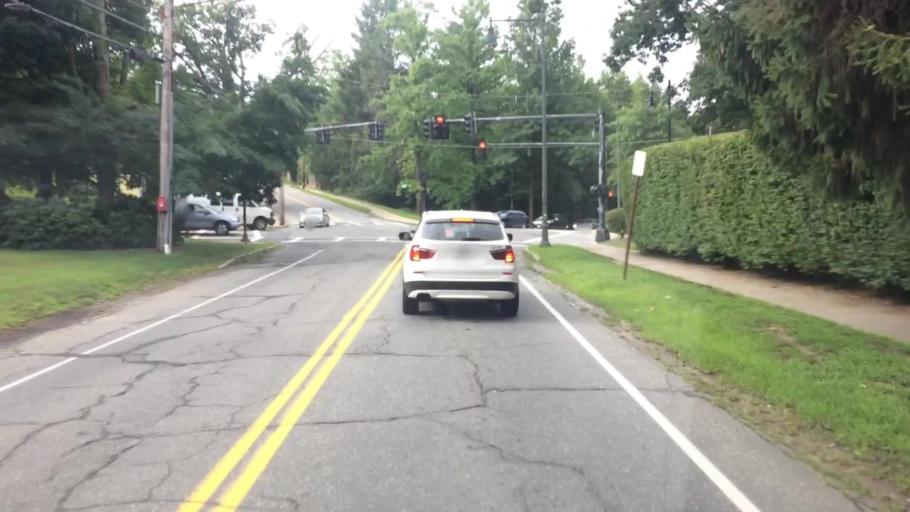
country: US
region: Massachusetts
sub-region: Middlesex County
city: Winchester
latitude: 42.4531
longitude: -71.1293
